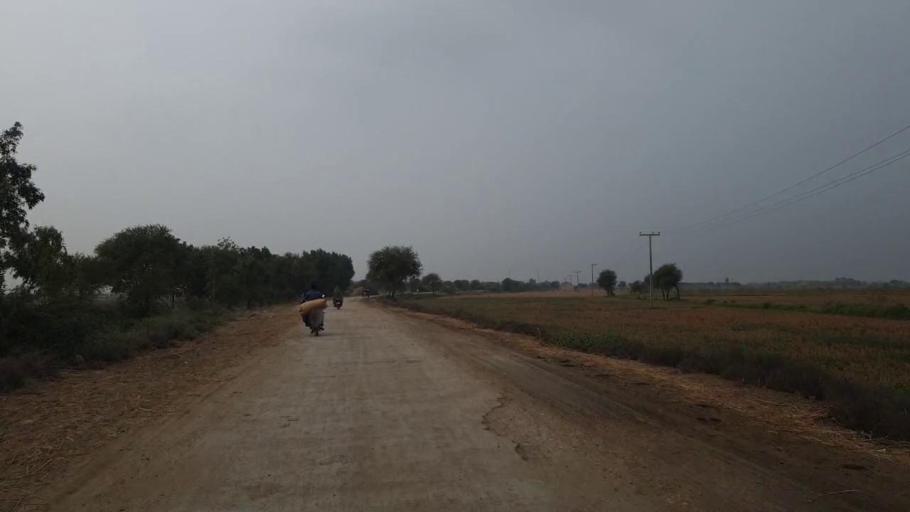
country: PK
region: Sindh
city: Kario
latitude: 24.9336
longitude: 68.5741
